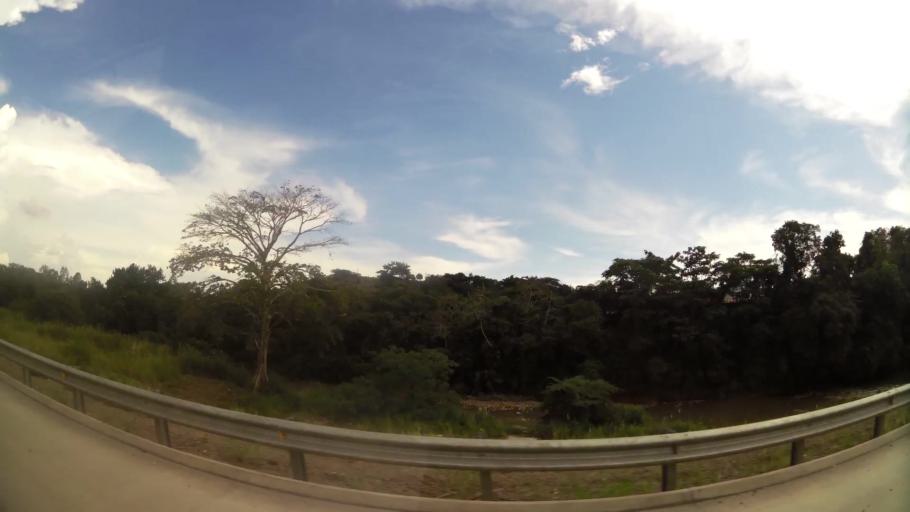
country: PA
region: Panama
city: San Miguelito
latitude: 9.0825
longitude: -79.4499
